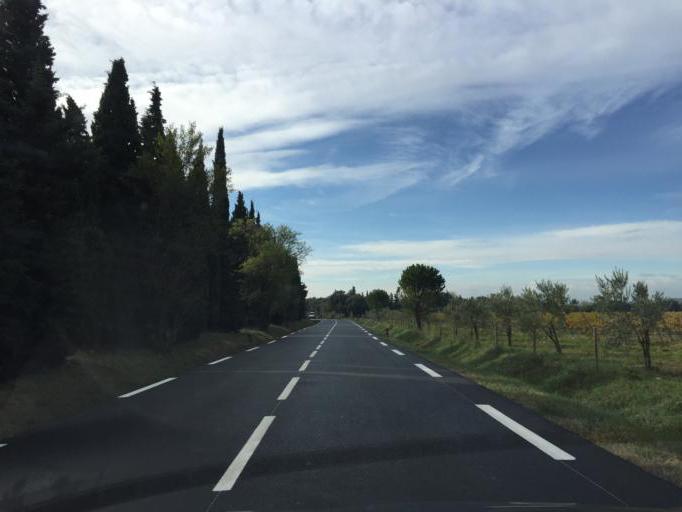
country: FR
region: Provence-Alpes-Cote d'Azur
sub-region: Departement du Vaucluse
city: Serignan-du-Comtat
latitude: 44.1744
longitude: 4.8170
